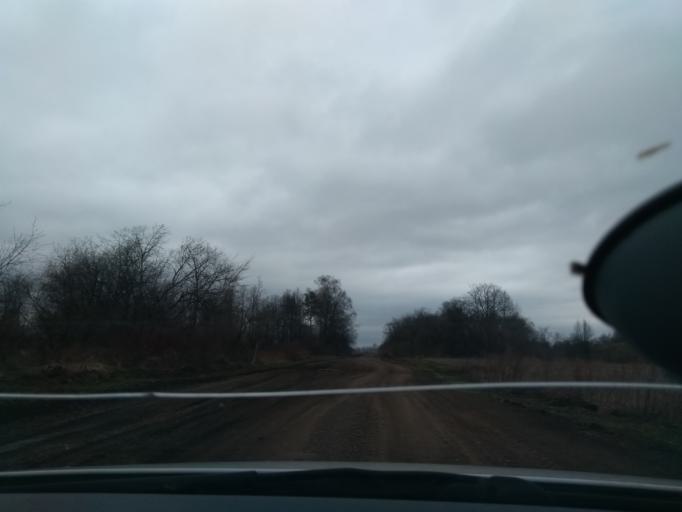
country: RU
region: Perm
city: Orda
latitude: 57.2412
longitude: 56.6109
